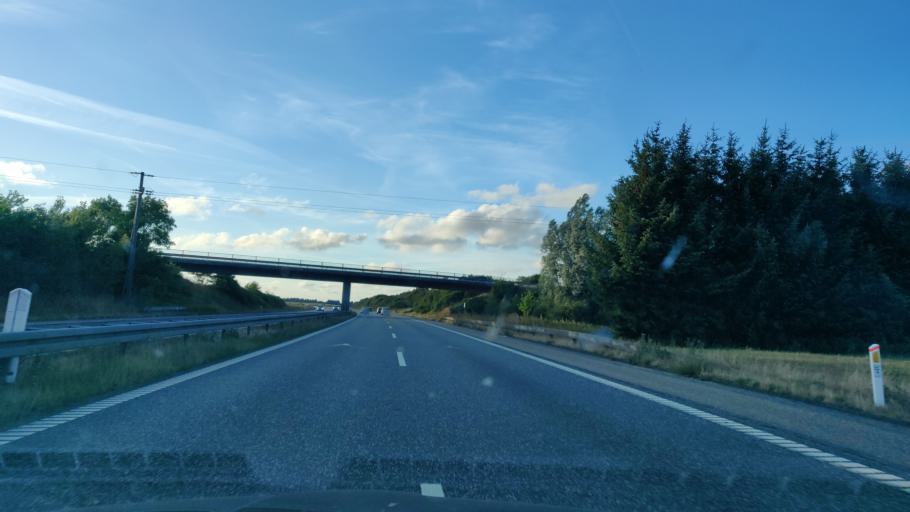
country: DK
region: North Denmark
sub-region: Mariagerfjord Kommune
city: Hobro
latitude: 56.7117
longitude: 9.7277
